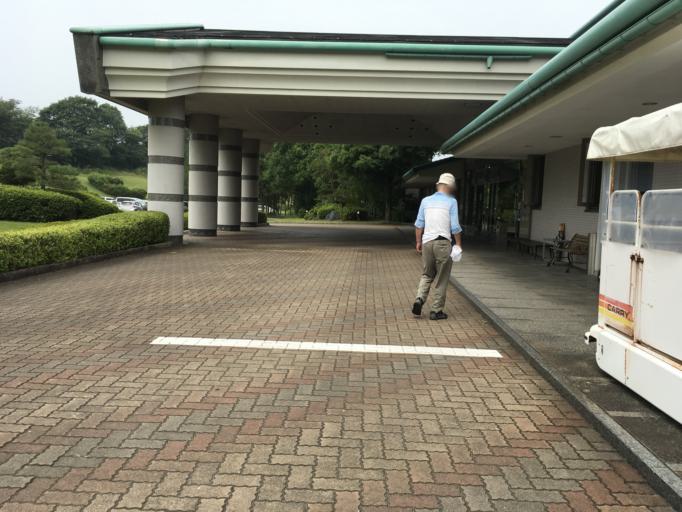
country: JP
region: Iwate
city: Ichinoseki
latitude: 38.8799
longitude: 141.0747
